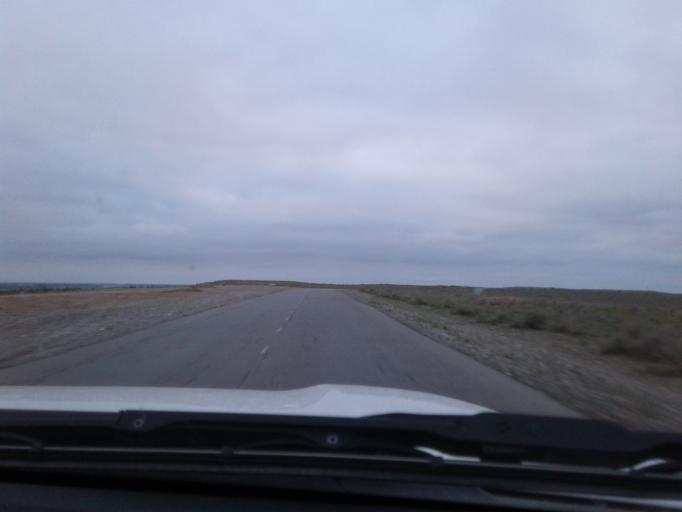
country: TM
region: Lebap
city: Turkmenabat
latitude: 39.0612
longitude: 63.7425
